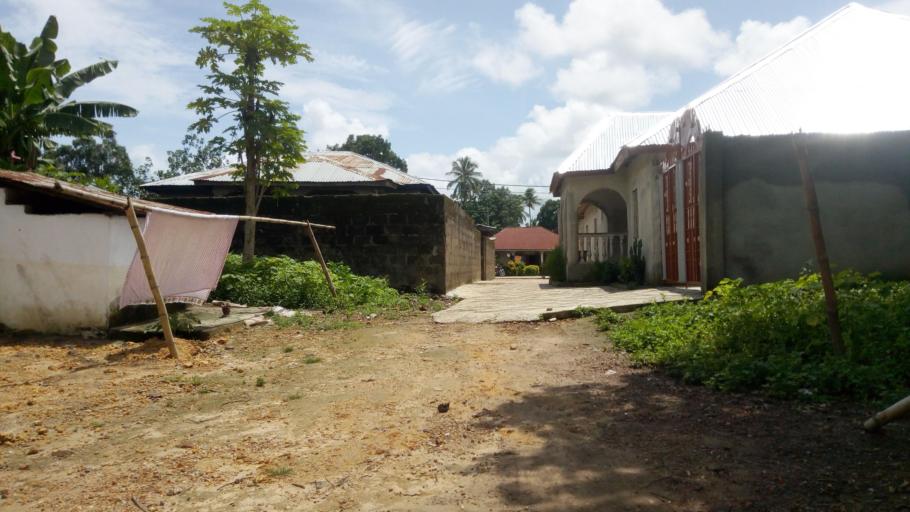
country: SL
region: Northern Province
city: Magburaka
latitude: 8.7195
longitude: -11.9560
